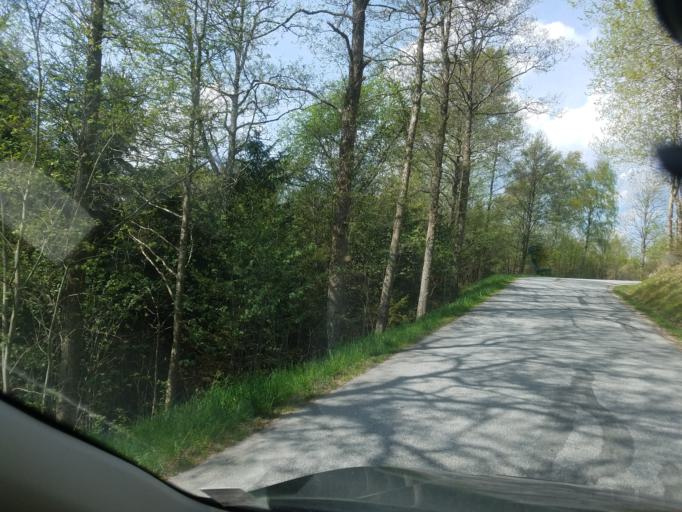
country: SE
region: Vaestra Goetaland
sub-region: Orust
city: Henan
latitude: 58.2735
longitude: 11.5727
